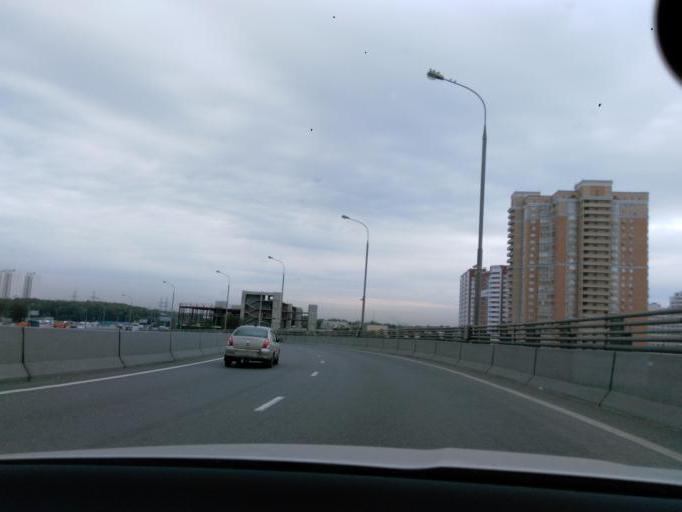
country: RU
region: Moscow
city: Vagonoremont
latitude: 55.9067
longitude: 37.5439
